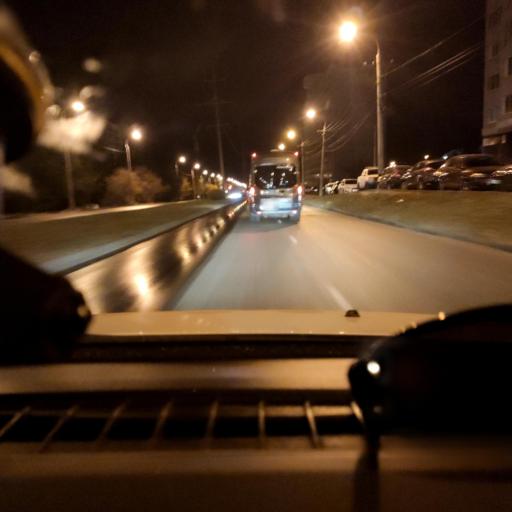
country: RU
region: Samara
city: Samara
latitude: 53.2092
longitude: 50.2133
